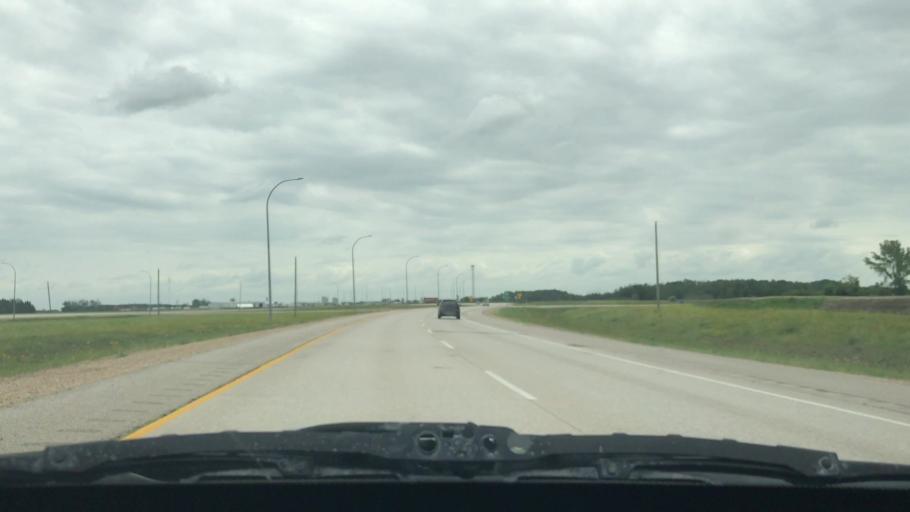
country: CA
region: Manitoba
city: Winnipeg
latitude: 49.8282
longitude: -96.9504
